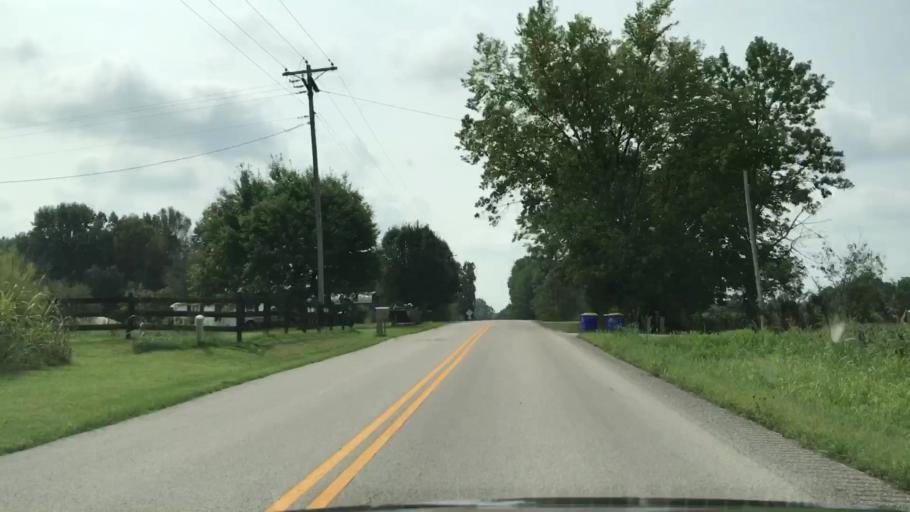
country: US
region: Kentucky
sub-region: Edmonson County
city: Brownsville
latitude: 37.1214
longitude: -86.1537
